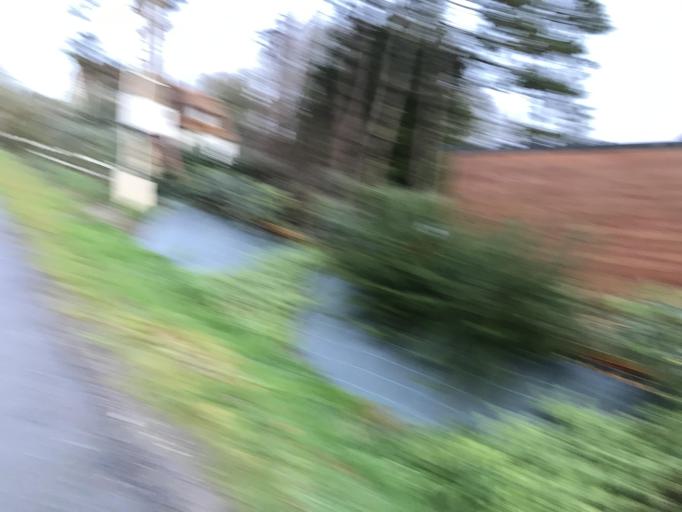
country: FR
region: Brittany
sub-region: Departement du Finistere
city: Logonna-Daoulas
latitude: 48.3182
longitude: -4.3159
